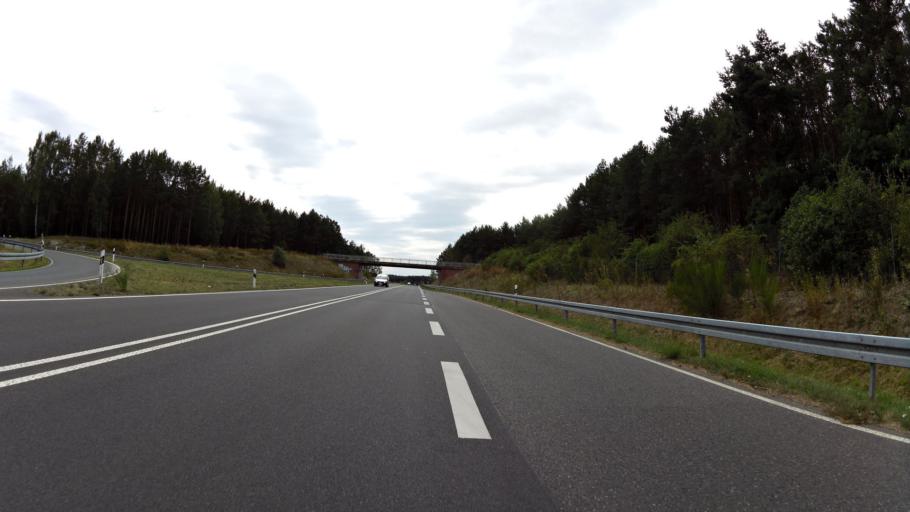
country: DE
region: Brandenburg
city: Schenkendobern
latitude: 51.9540
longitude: 14.6461
